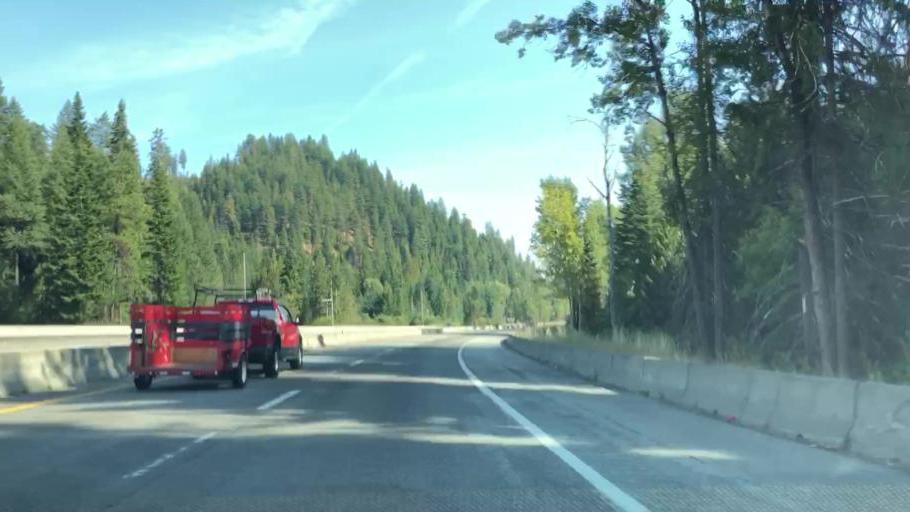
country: US
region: Idaho
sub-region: Shoshone County
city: Pinehurst
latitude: 47.5873
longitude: -116.4778
